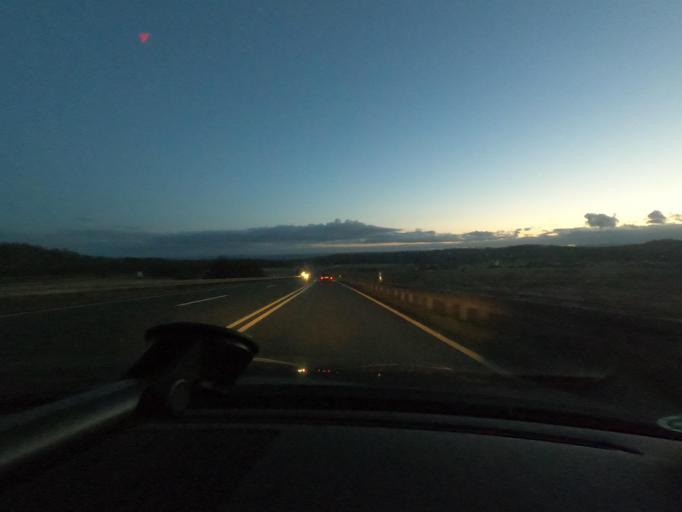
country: DE
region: Lower Saxony
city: Bad Sachsa
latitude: 51.5804
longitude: 10.5141
